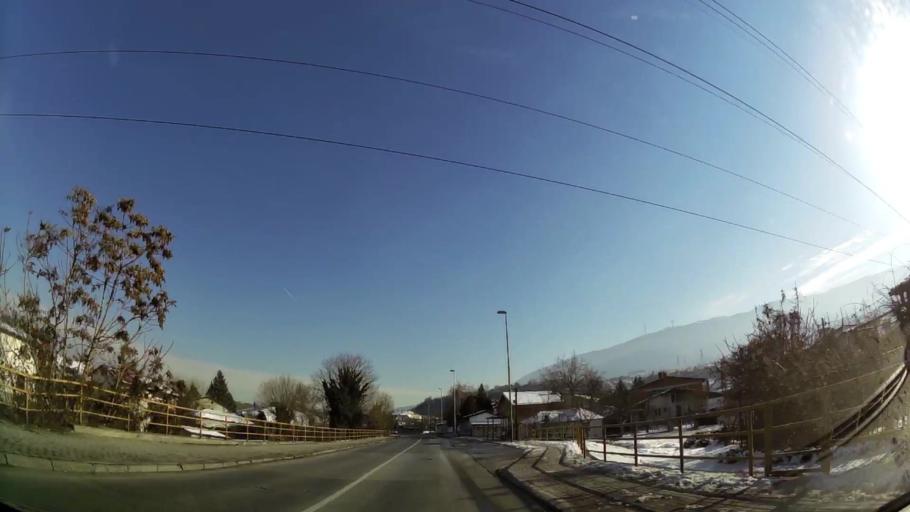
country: MK
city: Krushopek
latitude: 42.0009
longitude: 21.3779
